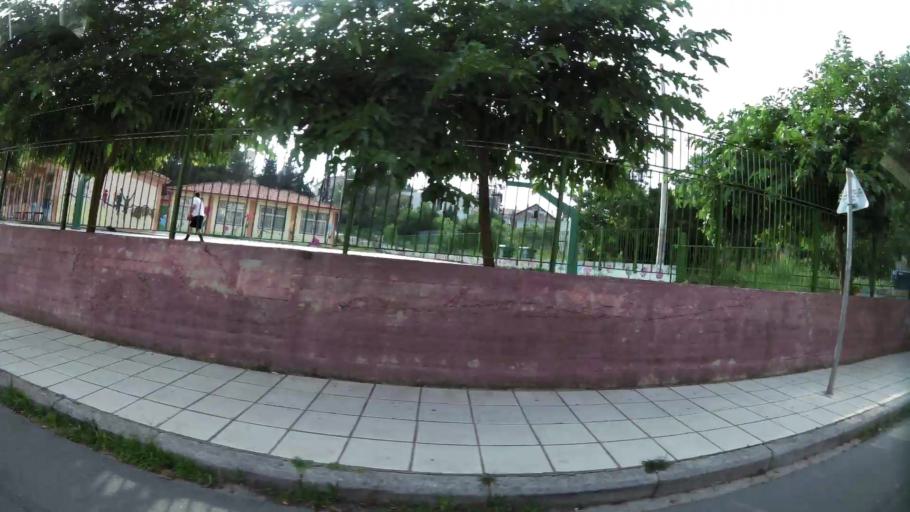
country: GR
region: Central Macedonia
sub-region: Nomos Thessalonikis
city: Oraiokastro
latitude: 40.7279
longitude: 22.9179
